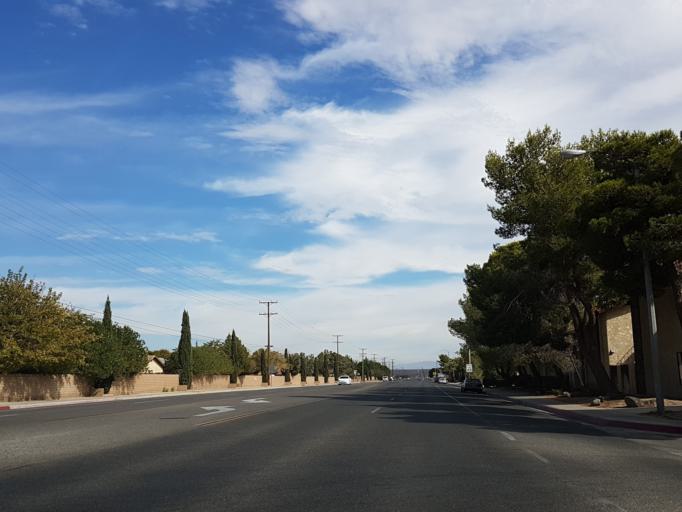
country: US
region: California
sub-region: Kern County
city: Ridgecrest
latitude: 35.6225
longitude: -117.6582
